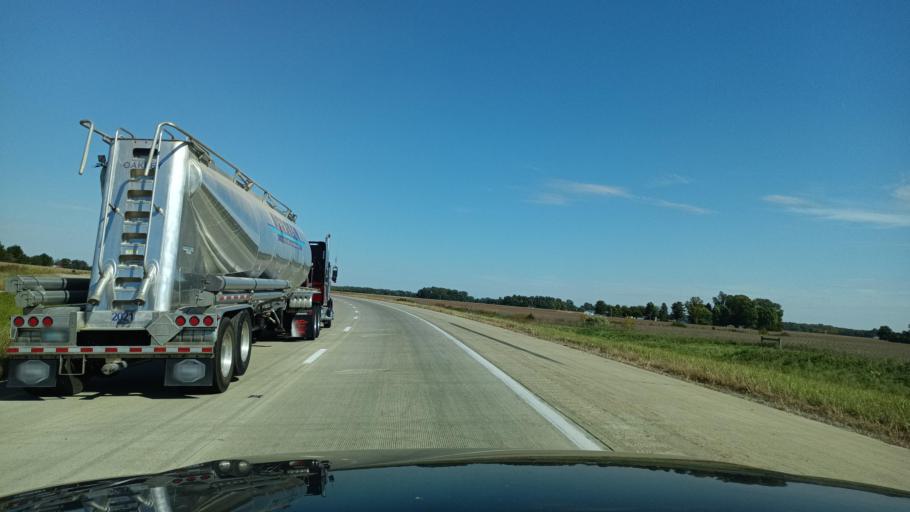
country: US
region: Ohio
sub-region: Lucas County
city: Whitehouse
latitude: 41.4401
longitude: -83.8464
